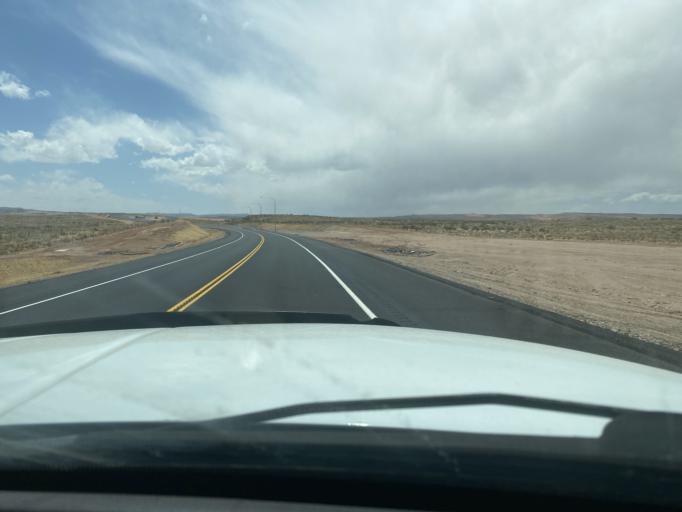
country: US
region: Utah
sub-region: Washington County
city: Hurricane
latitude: 37.1363
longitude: -113.3478
